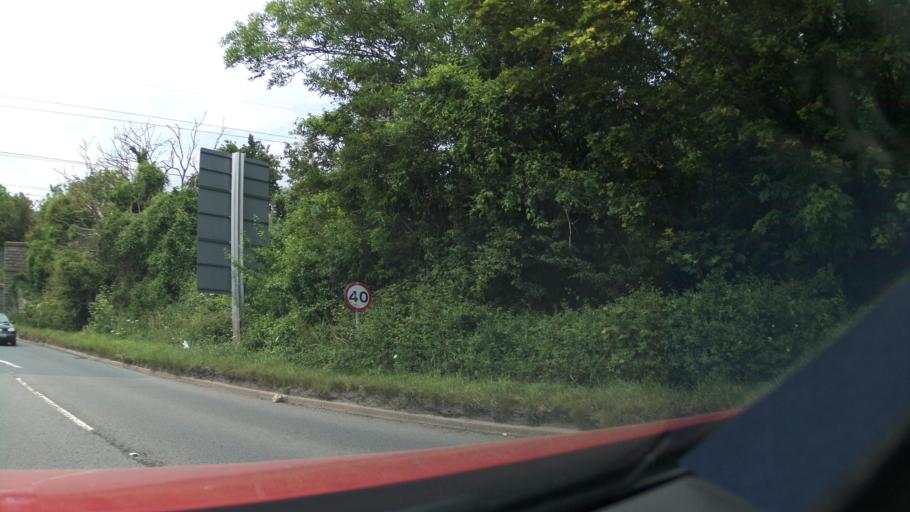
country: GB
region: Wales
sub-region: Vale of Glamorgan
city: Rhoose
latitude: 51.4006
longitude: -3.3935
